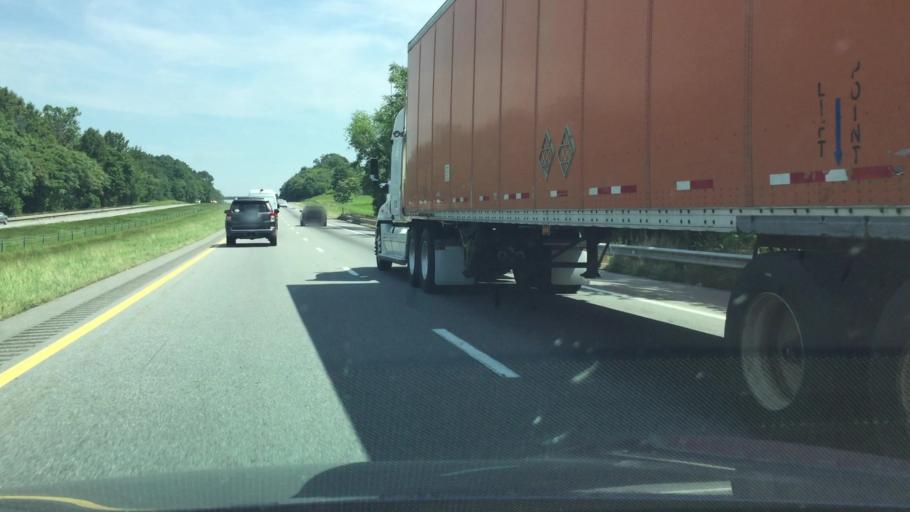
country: US
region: North Carolina
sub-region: Yadkin County
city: Yadkinville
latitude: 36.0622
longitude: -80.8223
